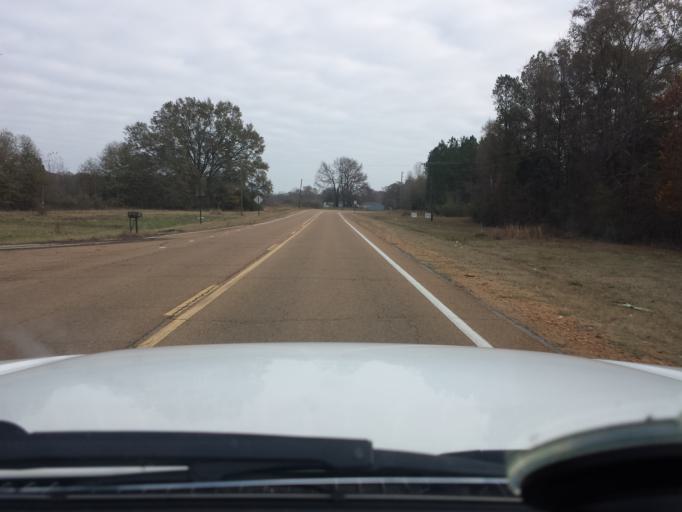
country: US
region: Mississippi
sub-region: Yazoo County
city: Yazoo City
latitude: 32.7897
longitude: -90.2047
